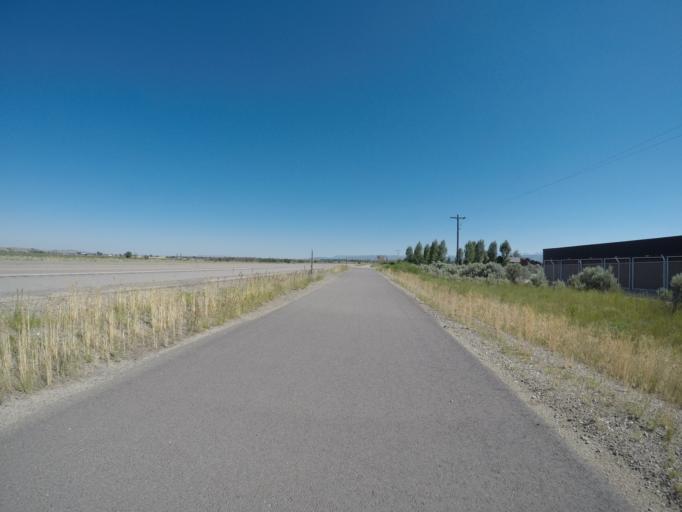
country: US
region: Wyoming
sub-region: Sublette County
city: Pinedale
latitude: 42.8385
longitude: -109.8465
